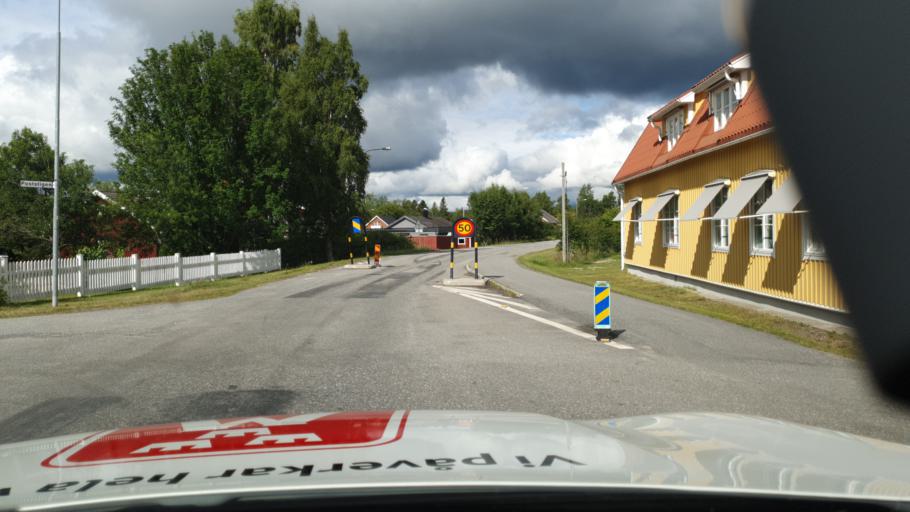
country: SE
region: Vaesterbotten
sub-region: Umea Kommun
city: Hoernefors
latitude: 63.6806
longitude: 20.0083
